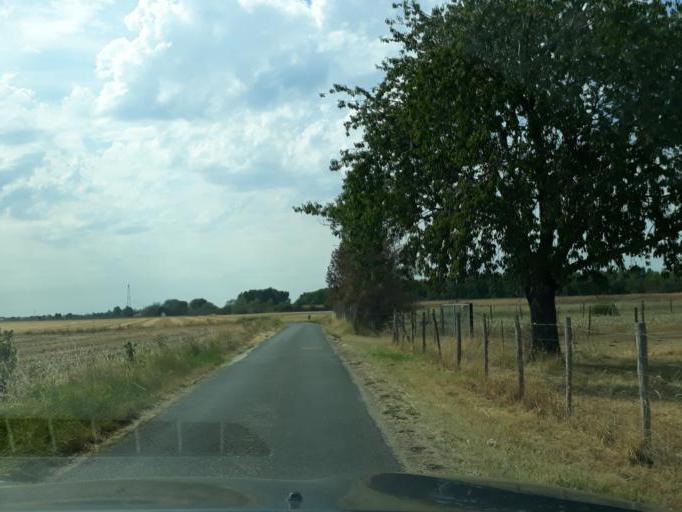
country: FR
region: Centre
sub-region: Departement du Loiret
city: Chateauneuf-sur-Loire
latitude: 47.8452
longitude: 2.2039
